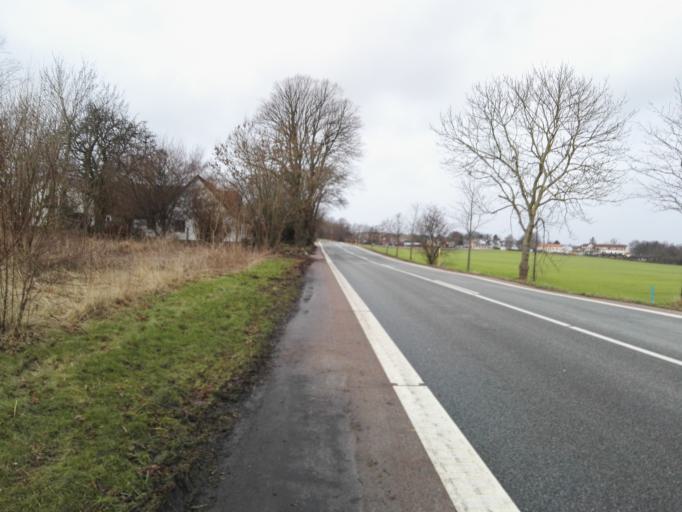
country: DK
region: Zealand
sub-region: Lejre Kommune
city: Ejby
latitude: 55.6807
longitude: 11.9255
